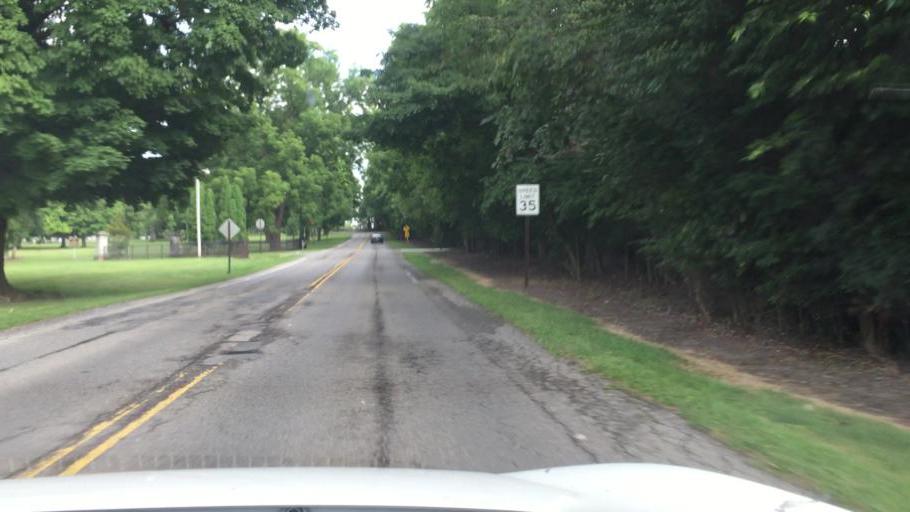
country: US
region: Ohio
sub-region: Champaign County
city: Urbana
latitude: 40.1029
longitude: -83.7367
